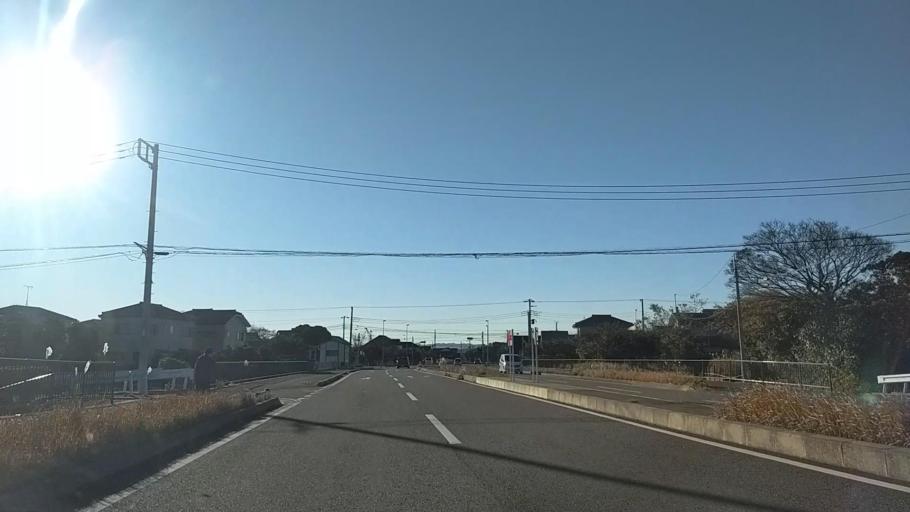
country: JP
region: Chiba
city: Kisarazu
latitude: 35.4008
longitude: 139.9205
